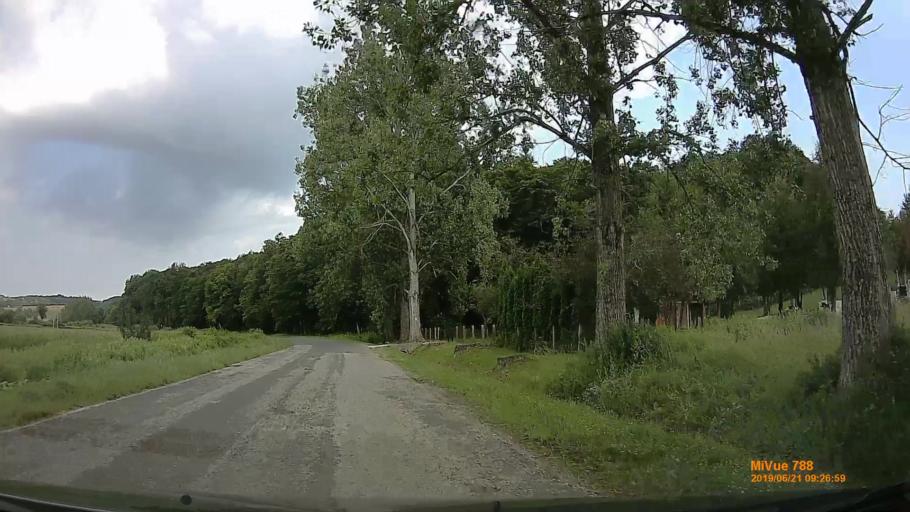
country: HU
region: Somogy
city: Taszar
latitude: 46.2754
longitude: 17.9016
